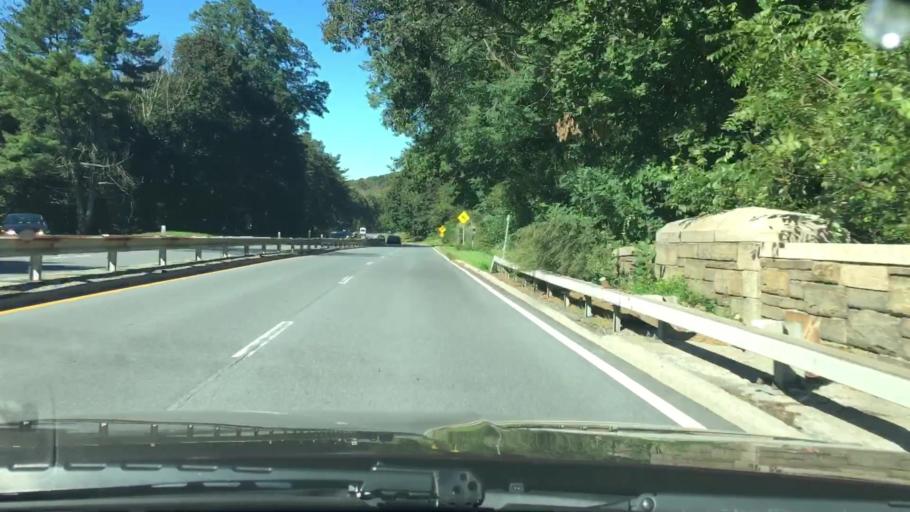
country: US
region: New York
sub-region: Westchester County
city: Mount Kisco
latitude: 41.2091
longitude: -73.7359
